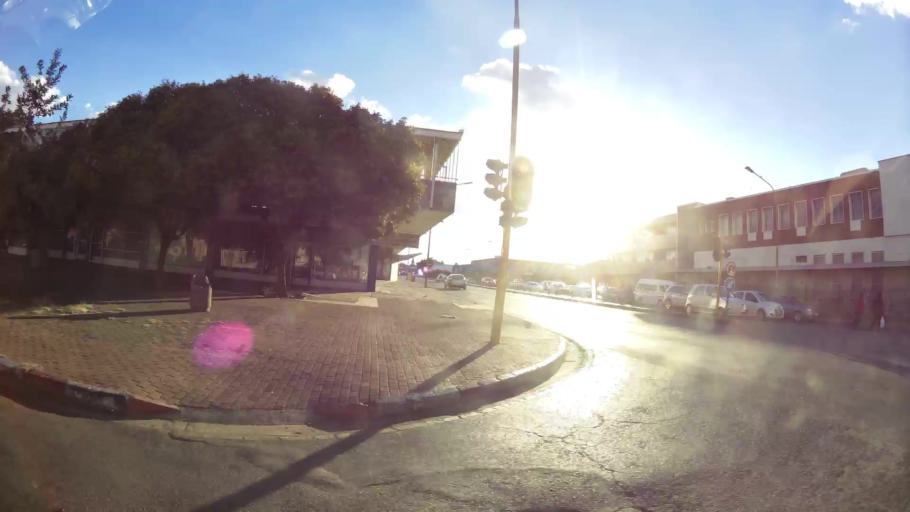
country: ZA
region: North-West
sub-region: Dr Kenneth Kaunda District Municipality
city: Potchefstroom
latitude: -26.7146
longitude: 27.0970
